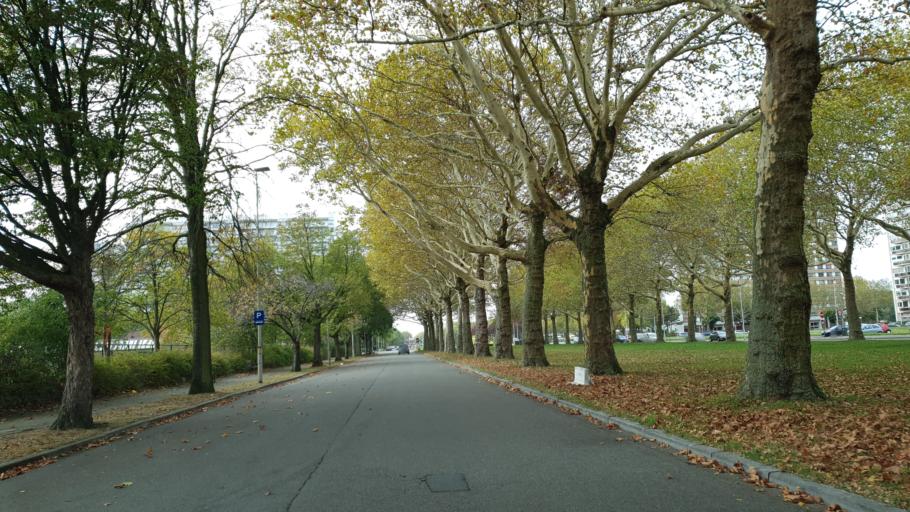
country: BE
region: Flanders
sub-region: Provincie Antwerpen
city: Antwerpen
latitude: 51.2271
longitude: 4.3894
